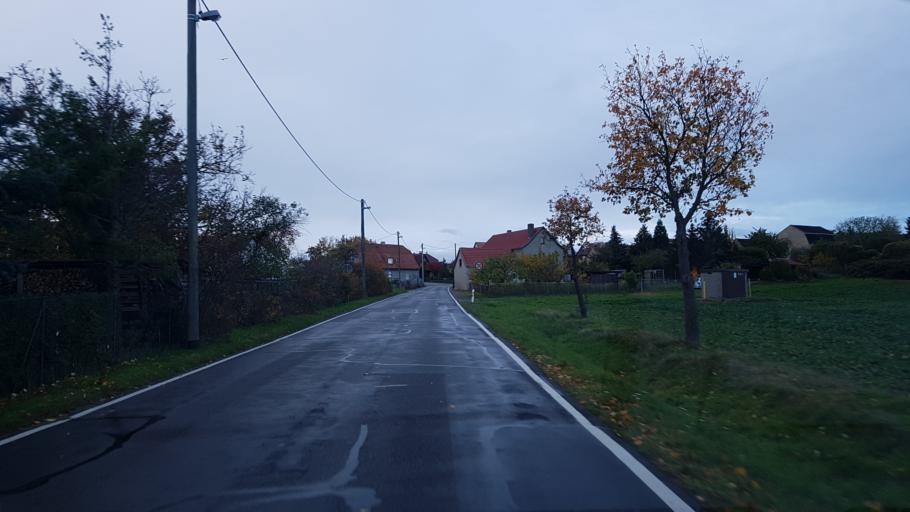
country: DE
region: Saxony
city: Belgern
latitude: 51.4527
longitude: 13.1153
